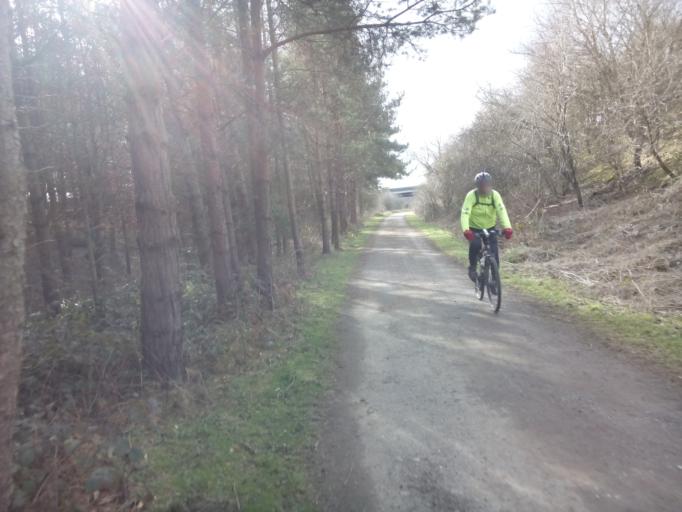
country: GB
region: England
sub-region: County Durham
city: Durham
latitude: 54.7711
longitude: -1.6060
